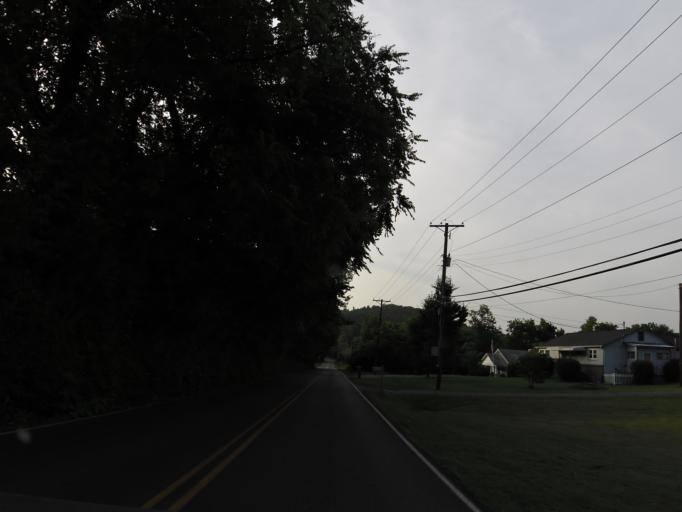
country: US
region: Tennessee
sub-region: Sevier County
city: Seymour
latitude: 35.8938
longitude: -83.7962
